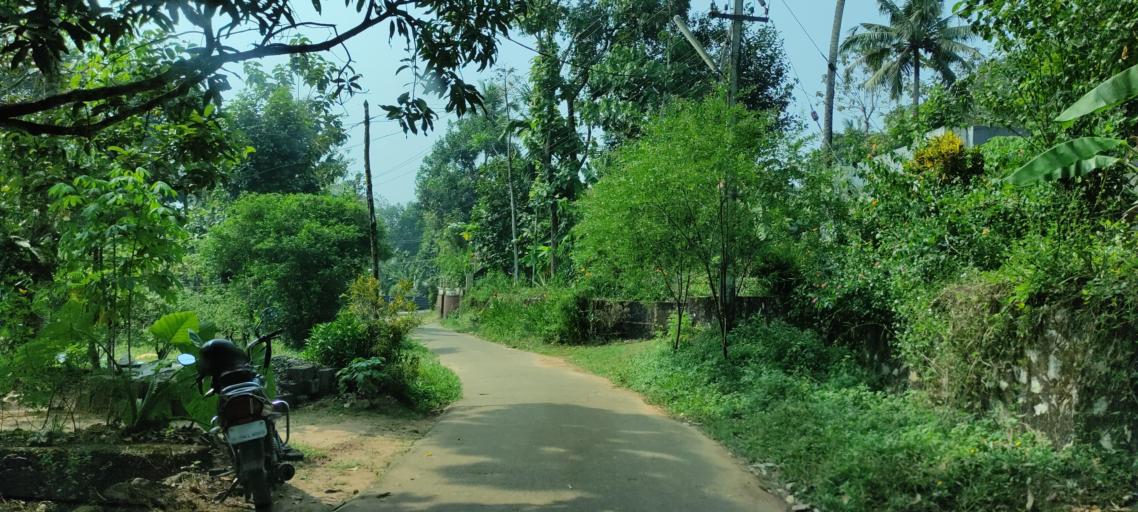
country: IN
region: Kerala
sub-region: Pattanamtitta
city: Adur
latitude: 9.2126
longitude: 76.6925
